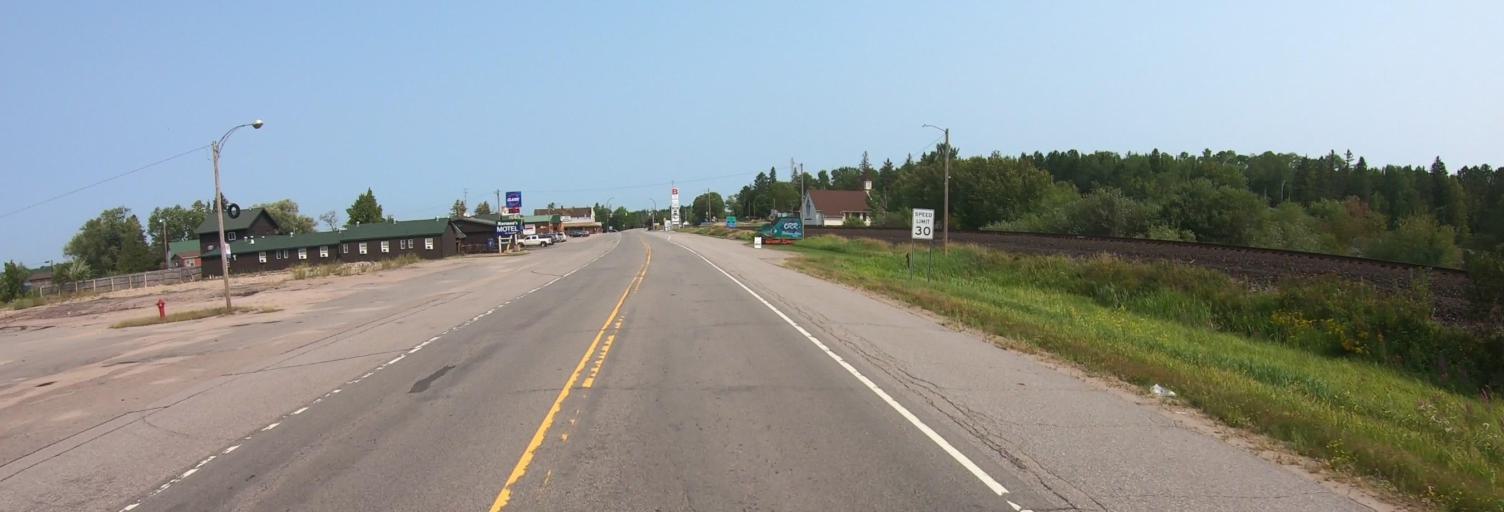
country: US
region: Minnesota
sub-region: Saint Louis County
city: Mountain Iron
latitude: 48.0508
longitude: -92.8319
